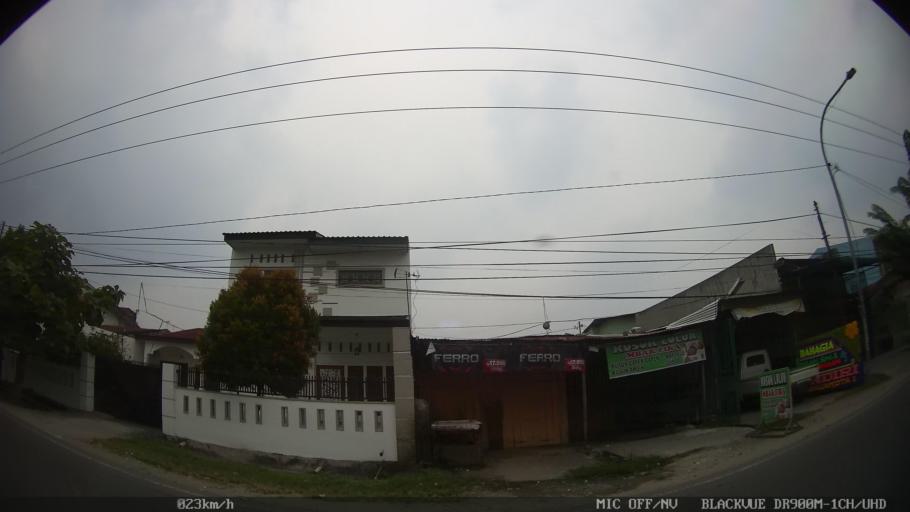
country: ID
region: North Sumatra
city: Medan
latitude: 3.5649
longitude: 98.7220
